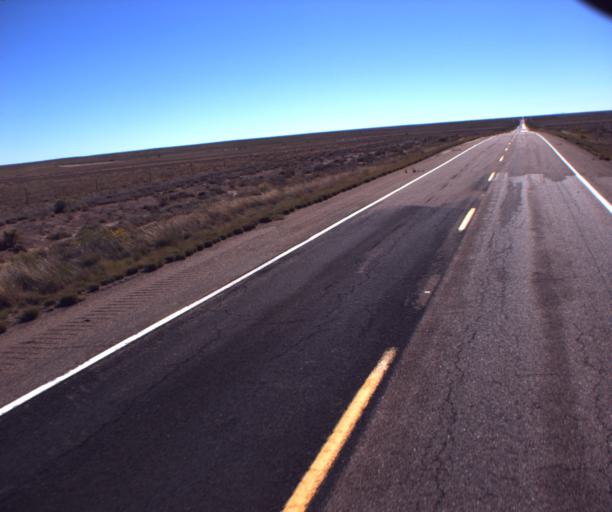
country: US
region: Arizona
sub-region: Navajo County
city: Snowflake
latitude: 34.7670
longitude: -109.8178
